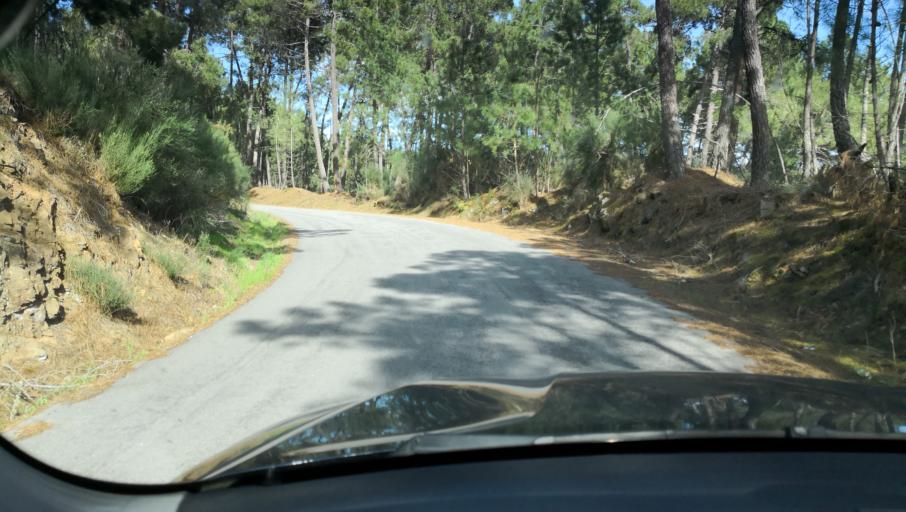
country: PT
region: Vila Real
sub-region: Vila Real
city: Vila Real
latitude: 41.2778
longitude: -7.6742
